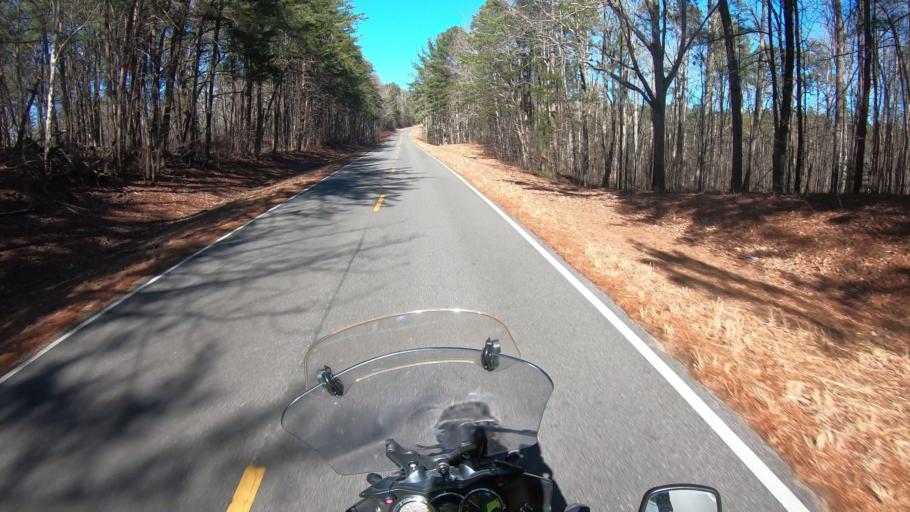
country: US
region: Alabama
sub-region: Calhoun County
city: Oxford
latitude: 33.5006
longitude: -85.7661
